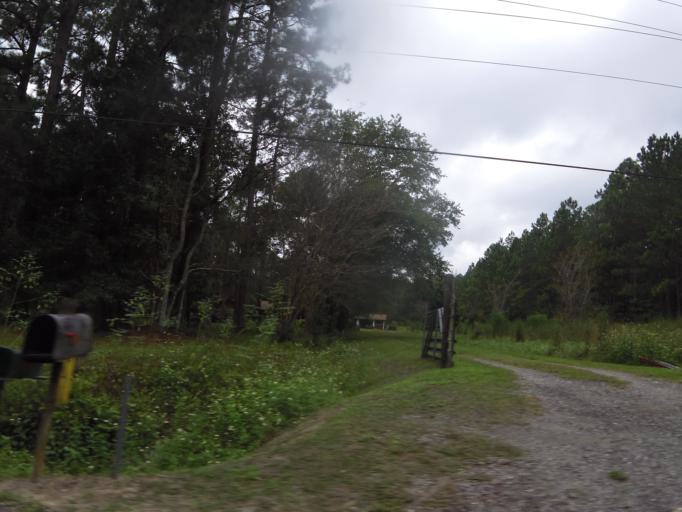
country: US
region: Florida
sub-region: Clay County
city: Middleburg
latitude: 30.1201
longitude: -81.9492
